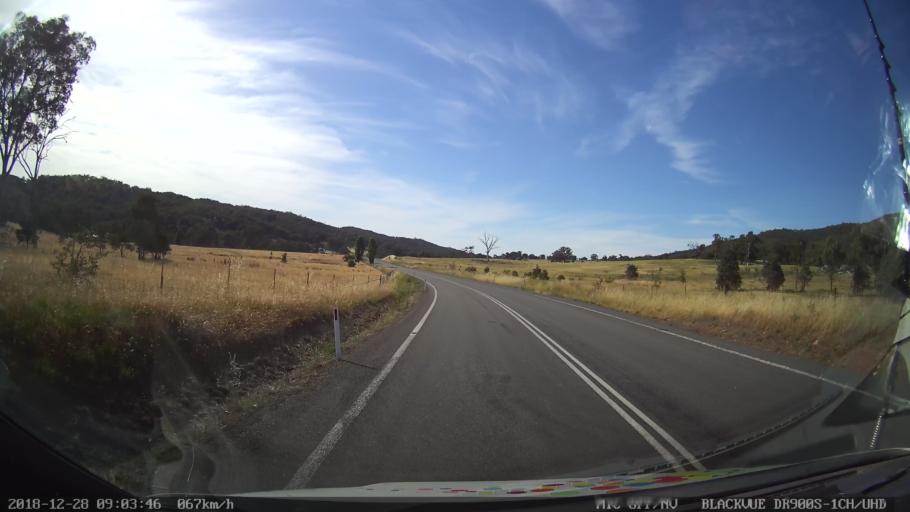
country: AU
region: New South Wales
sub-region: Upper Lachlan Shire
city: Crookwell
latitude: -34.1665
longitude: 149.3391
